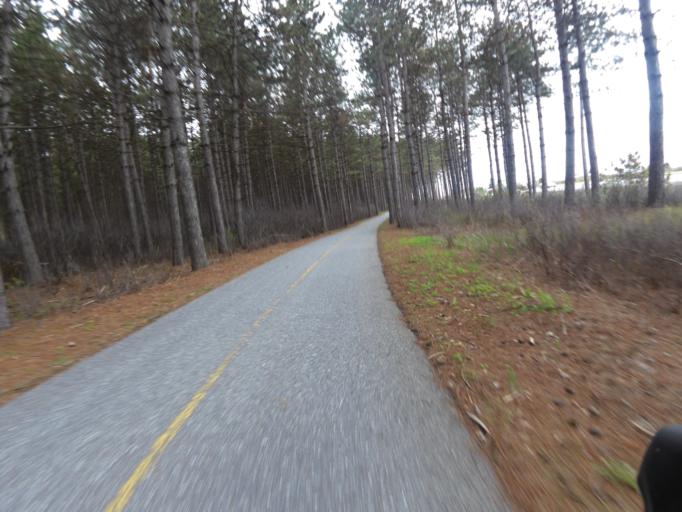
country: CA
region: Ontario
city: Bells Corners
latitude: 45.3168
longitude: -75.7412
